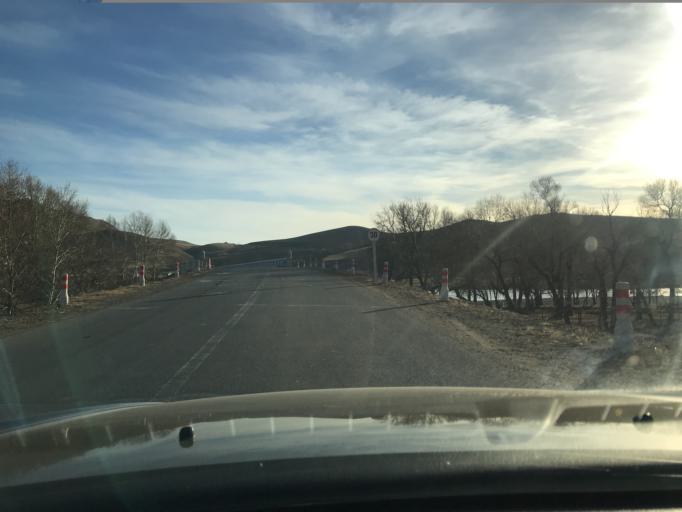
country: MN
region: Central Aimak
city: Dzuunmod
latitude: 47.8232
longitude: 107.3313
